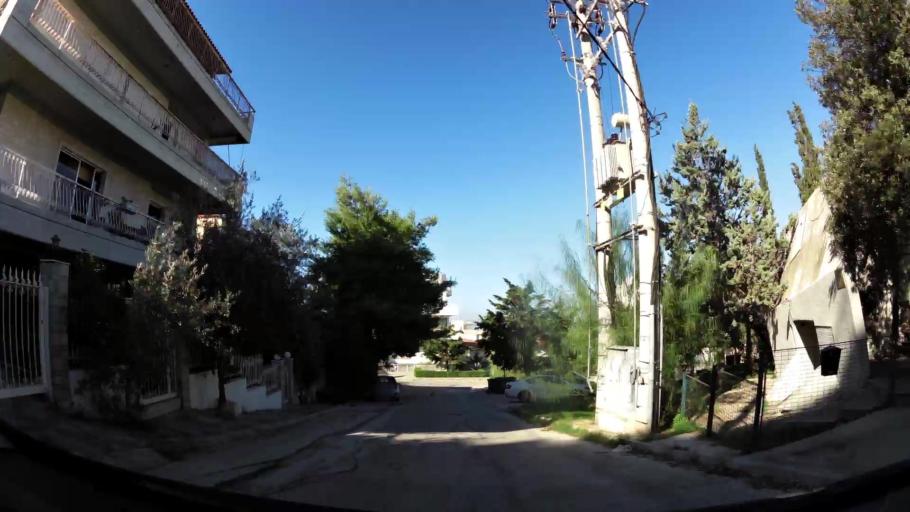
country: GR
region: Attica
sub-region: Nomarchia Anatolikis Attikis
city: Voula
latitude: 37.8563
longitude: 23.7720
